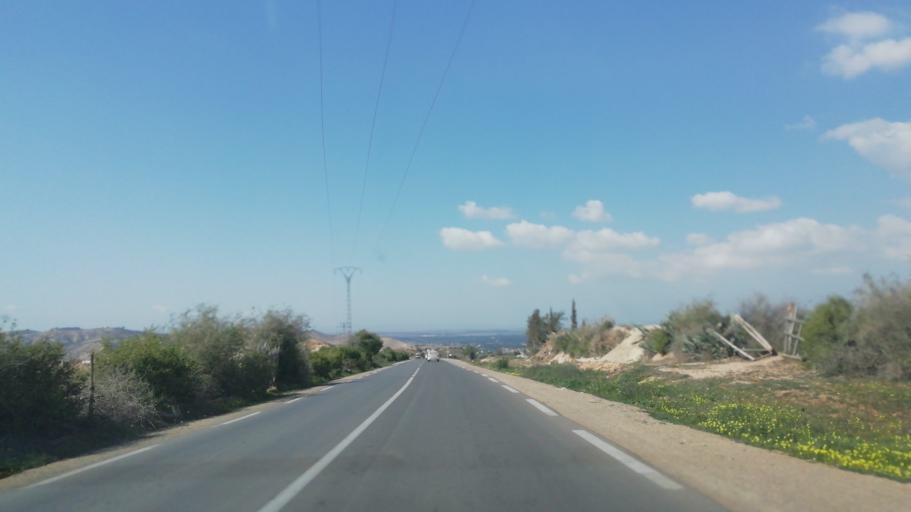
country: DZ
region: Mascara
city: Mascara
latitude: 35.5527
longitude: 0.0827
